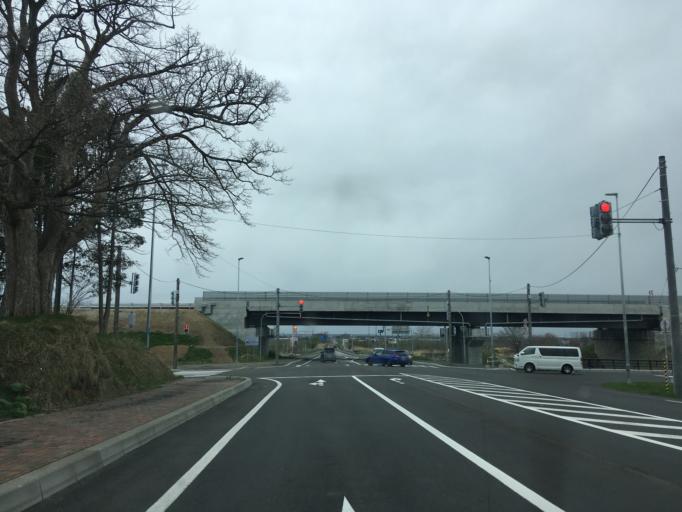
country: JP
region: Hokkaido
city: Chitose
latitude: 42.9506
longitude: 141.7160
